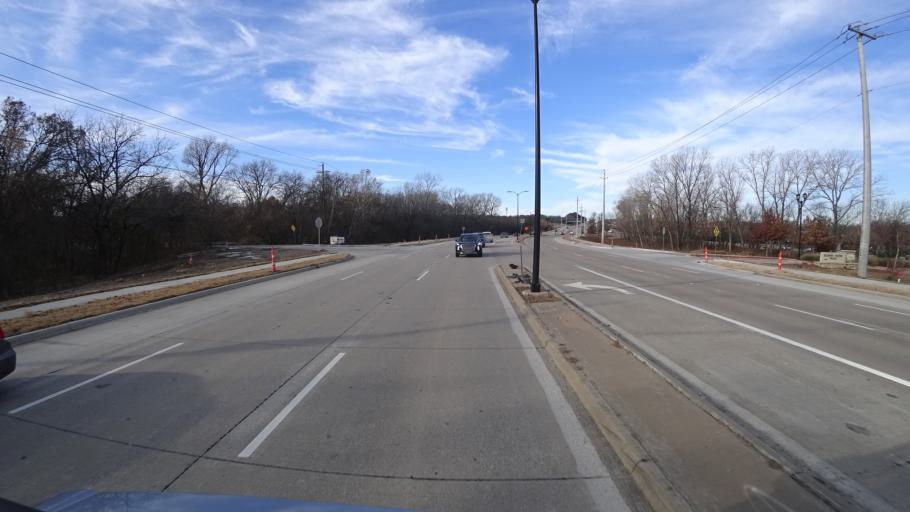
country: US
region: Texas
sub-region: Collin County
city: McKinney
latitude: 33.1965
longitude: -96.6614
